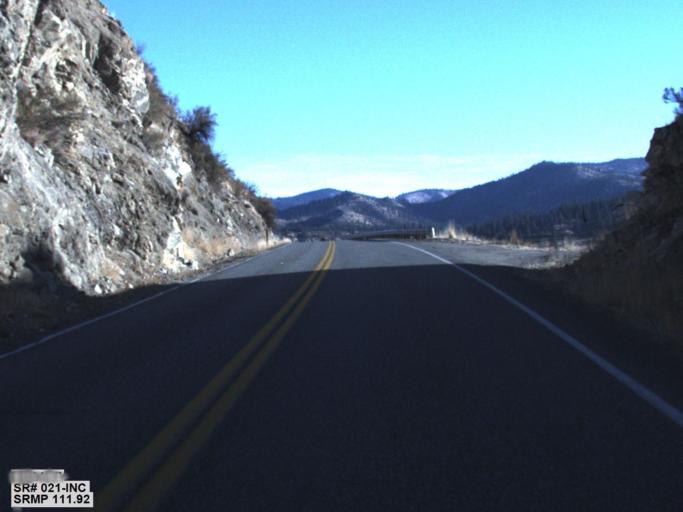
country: US
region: Washington
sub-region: Okanogan County
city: Coulee Dam
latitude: 48.0151
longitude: -118.6779
